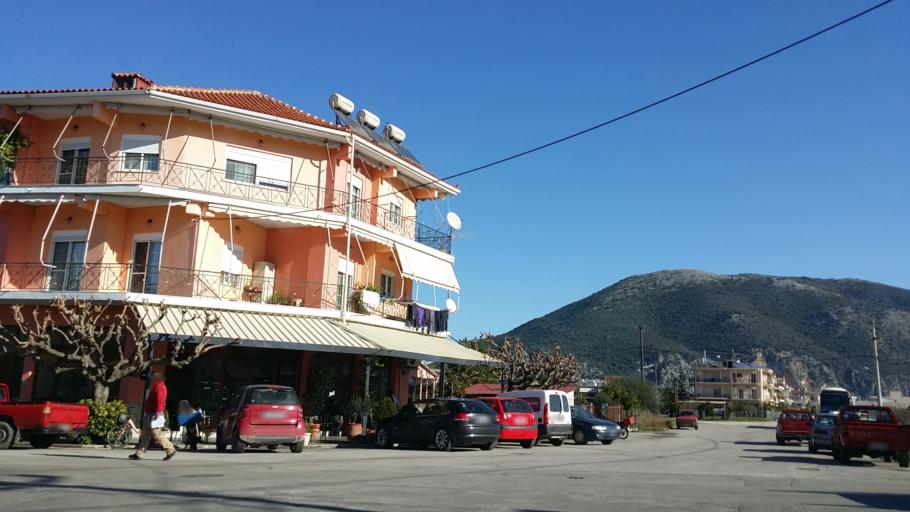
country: GR
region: West Greece
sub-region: Nomos Aitolias kai Akarnanias
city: Vonitsa
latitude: 38.9140
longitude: 20.8904
